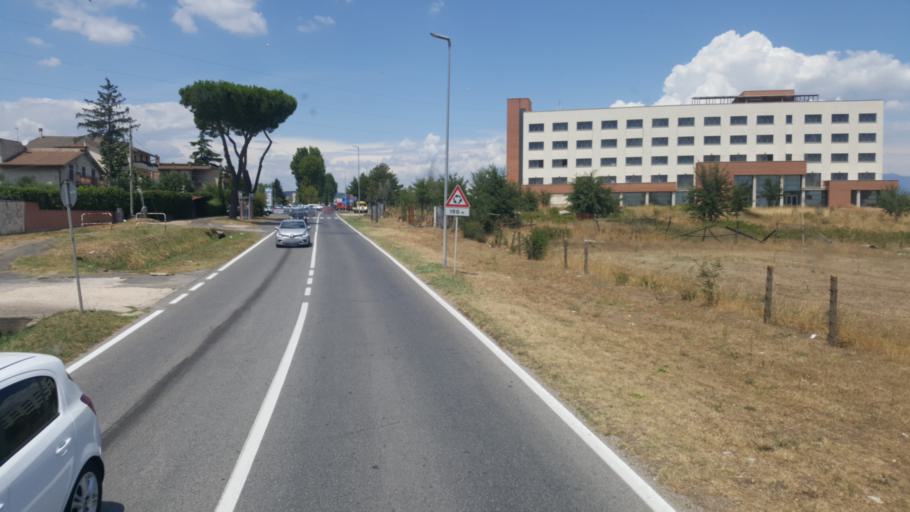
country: IT
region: Latium
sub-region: Citta metropolitana di Roma Capitale
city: Bivio di Capanelle
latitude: 42.1346
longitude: 12.5981
